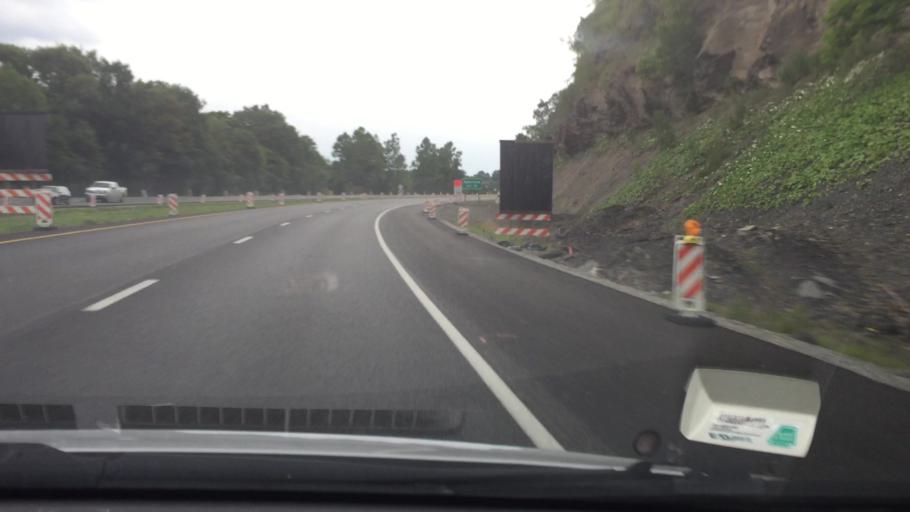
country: US
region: Pennsylvania
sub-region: Allegheny County
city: Brackenridge
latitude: 40.6428
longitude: -79.7202
